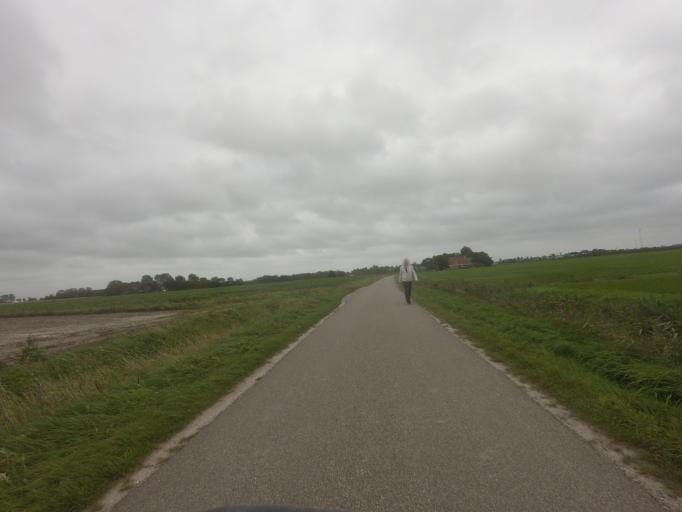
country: NL
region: Friesland
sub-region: Gemeente Leeuwarderadeel
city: Stiens
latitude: 53.2729
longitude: 5.7515
